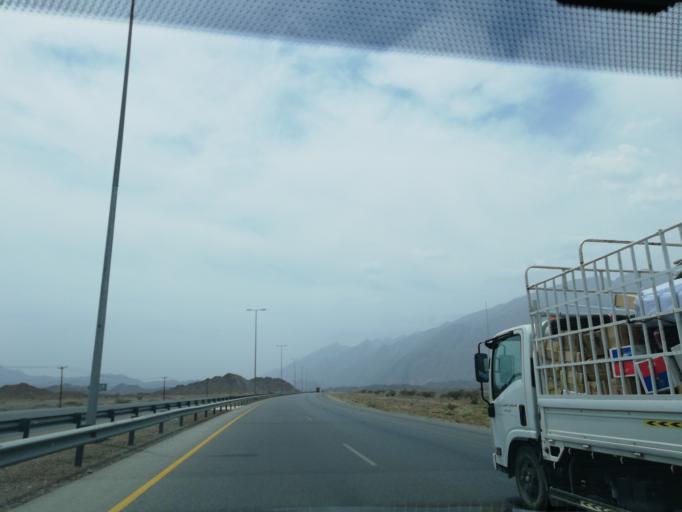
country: OM
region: Muhafazat ad Dakhiliyah
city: Sufalat Sama'il
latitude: 23.2444
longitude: 57.9166
